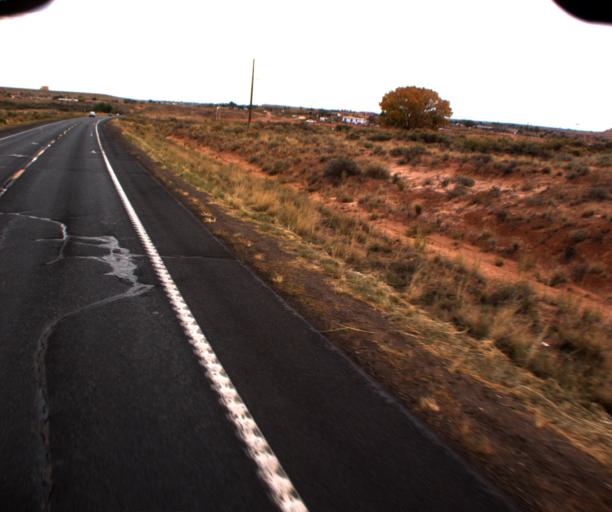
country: US
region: Arizona
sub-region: Coconino County
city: Tuba City
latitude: 36.1249
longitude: -111.2028
